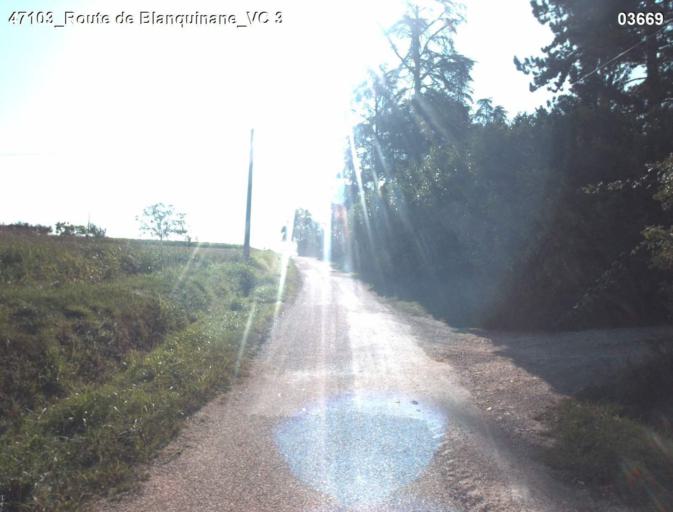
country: FR
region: Aquitaine
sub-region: Departement du Lot-et-Garonne
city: Nerac
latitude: 44.0912
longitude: 0.3226
